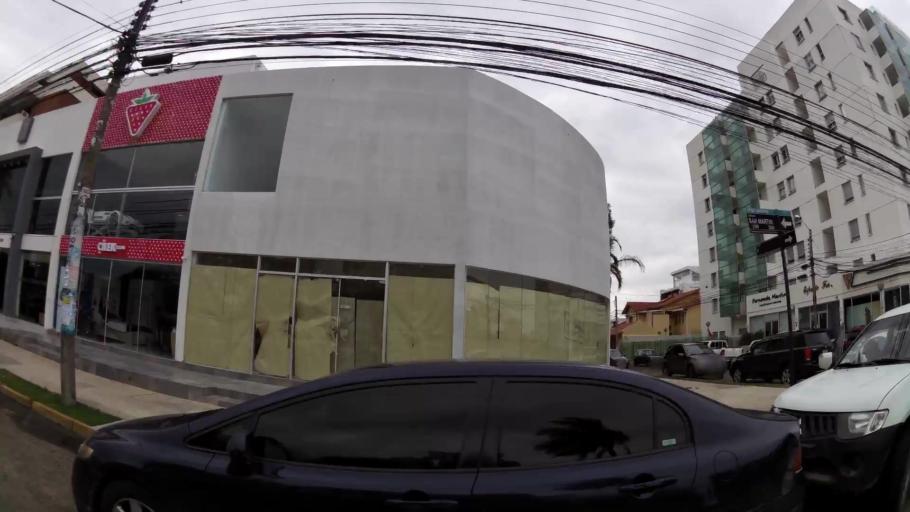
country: BO
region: Santa Cruz
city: Santa Cruz de la Sierra
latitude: -17.7591
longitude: -63.1994
